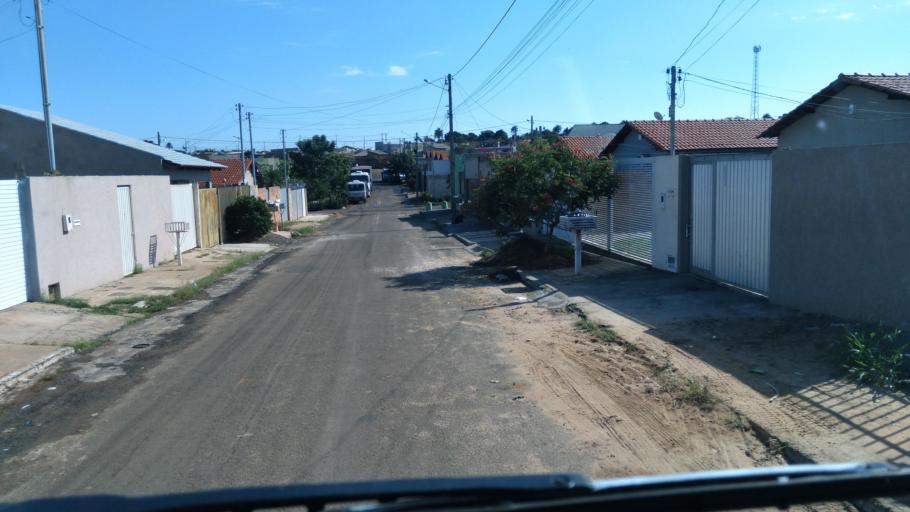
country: BR
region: Goias
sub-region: Mineiros
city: Mineiros
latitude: -17.5744
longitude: -52.5753
